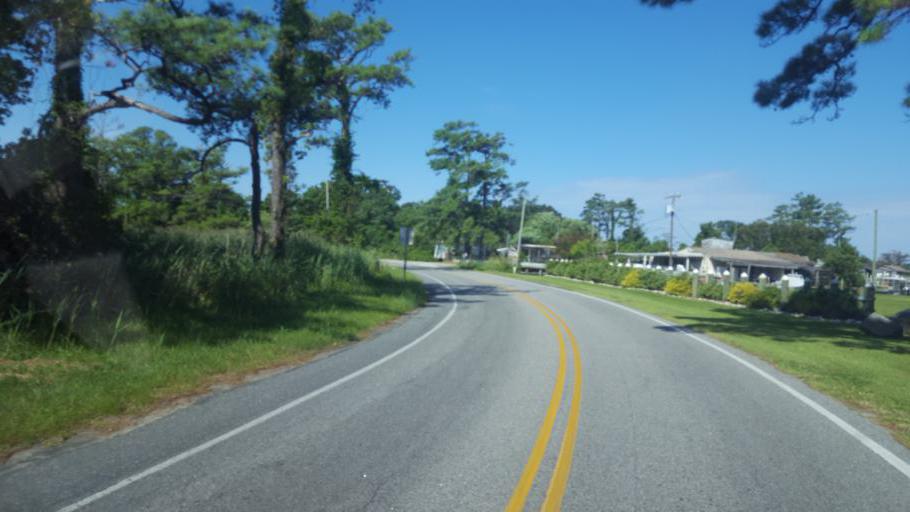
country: US
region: North Carolina
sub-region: Dare County
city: Kill Devil Hills
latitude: 36.0126
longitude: -75.6973
